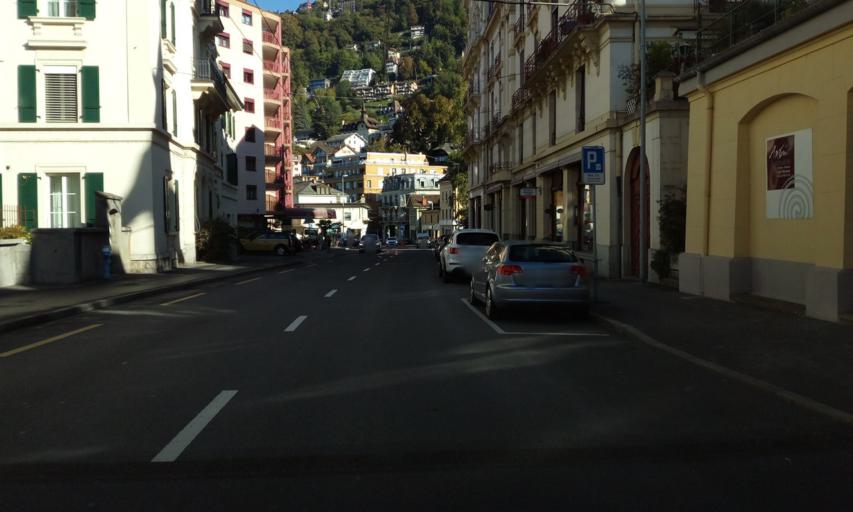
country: CH
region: Vaud
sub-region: Riviera-Pays-d'Enhaut District
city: Caux
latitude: 46.4225
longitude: 6.9254
